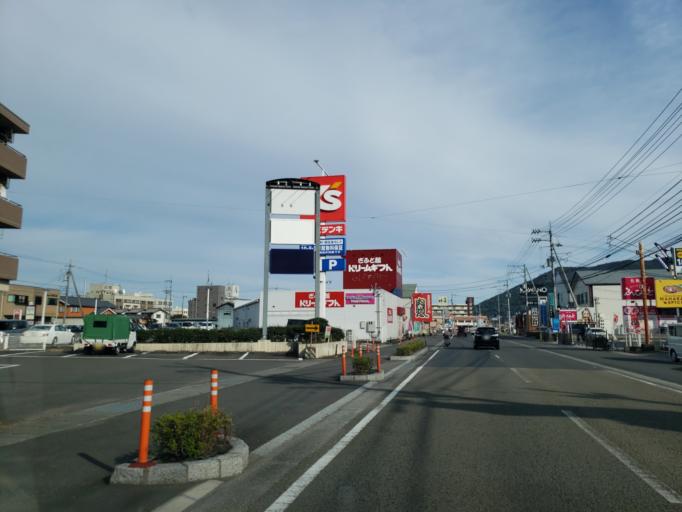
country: JP
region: Tokushima
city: Wakimachi
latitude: 34.0641
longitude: 134.1596
